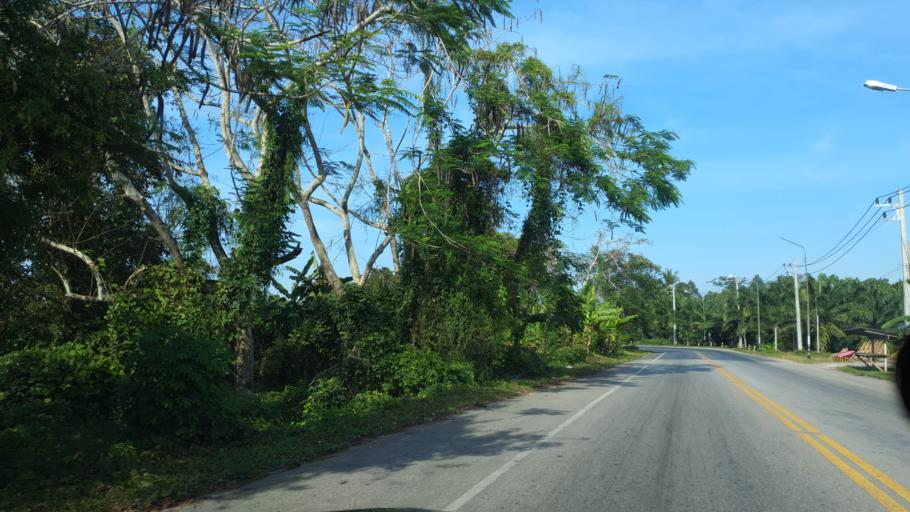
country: TH
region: Surat Thani
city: Ban Na Doem
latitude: 8.9348
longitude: 99.2681
